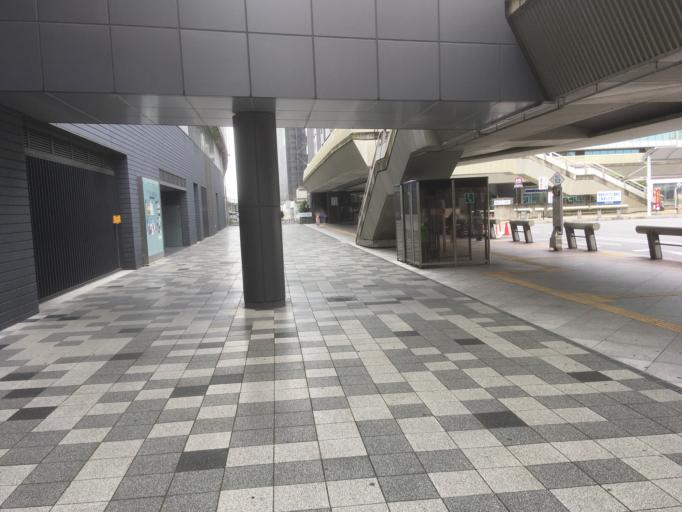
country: JP
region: Nara
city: Nara-shi
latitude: 34.6810
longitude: 135.8188
